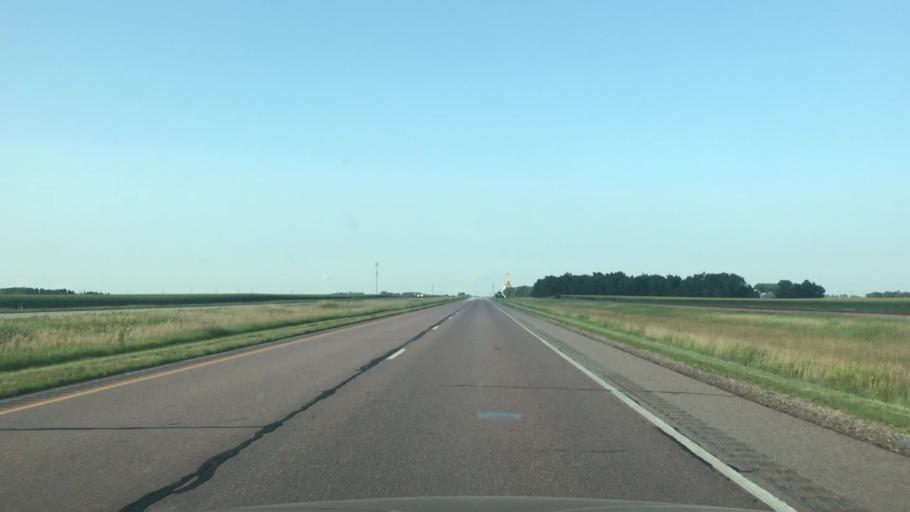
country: US
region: Minnesota
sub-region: Jackson County
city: Lakefield
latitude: 43.7549
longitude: -95.3847
